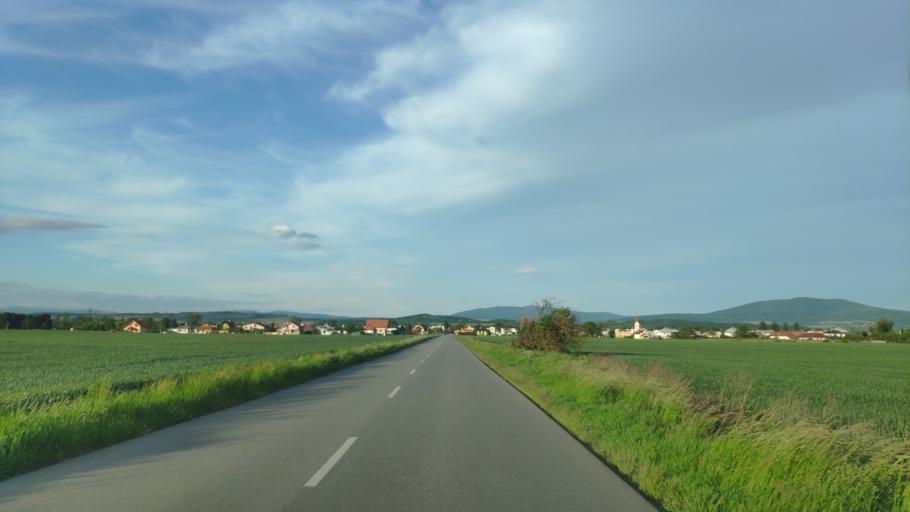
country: SK
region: Kosicky
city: Kosice
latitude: 48.6456
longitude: 21.3136
